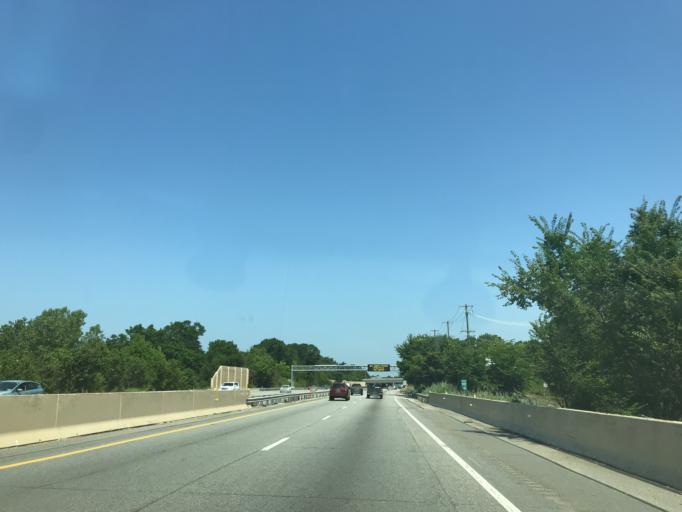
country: US
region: Pennsylvania
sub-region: Montgomery County
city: King of Prussia
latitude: 40.0861
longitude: -75.4117
